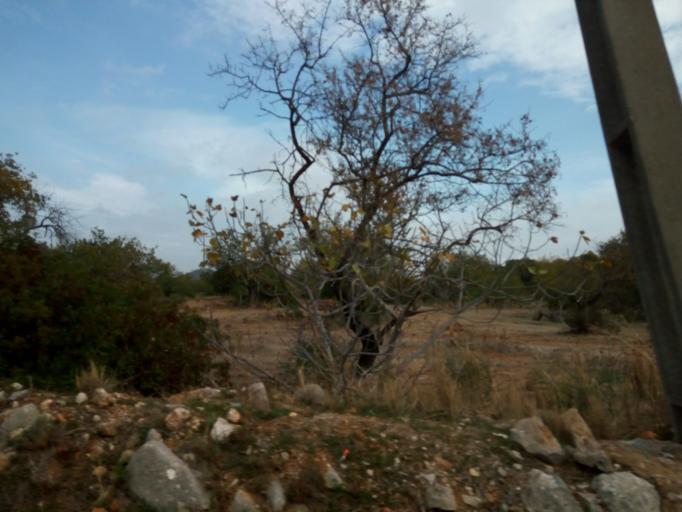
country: PT
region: Faro
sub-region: Faro
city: Santa Barbara de Nexe
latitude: 37.0975
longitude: -7.9638
